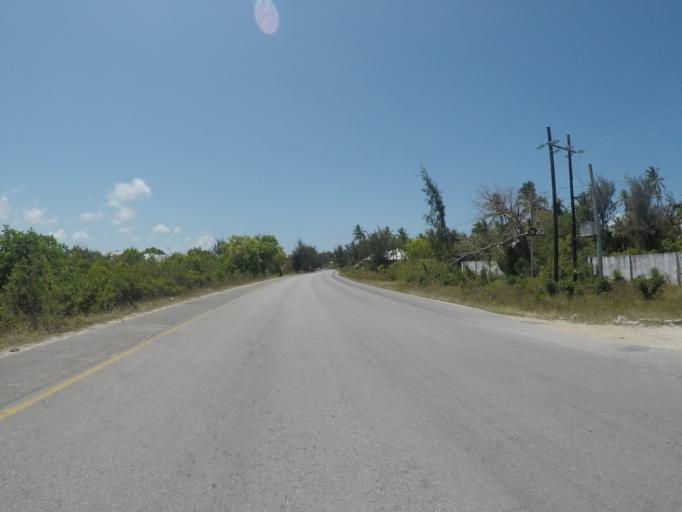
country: TZ
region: Zanzibar Central/South
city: Nganane
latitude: -6.2722
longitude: 39.5327
